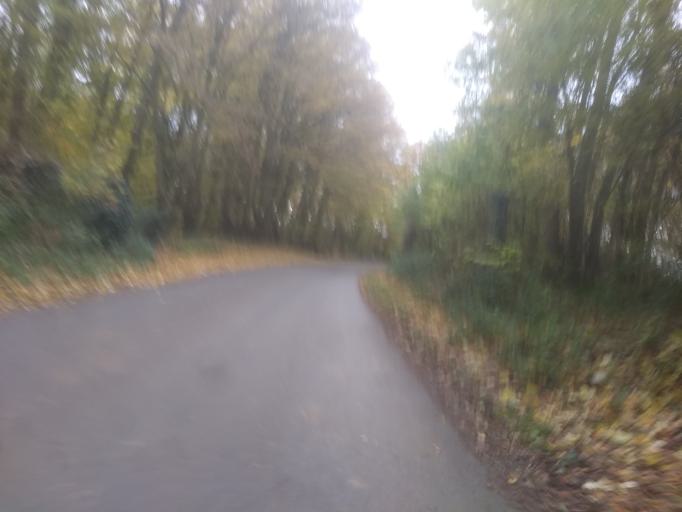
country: FR
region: Nord-Pas-de-Calais
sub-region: Departement du Pas-de-Calais
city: Dainville
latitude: 50.2576
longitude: 2.7188
